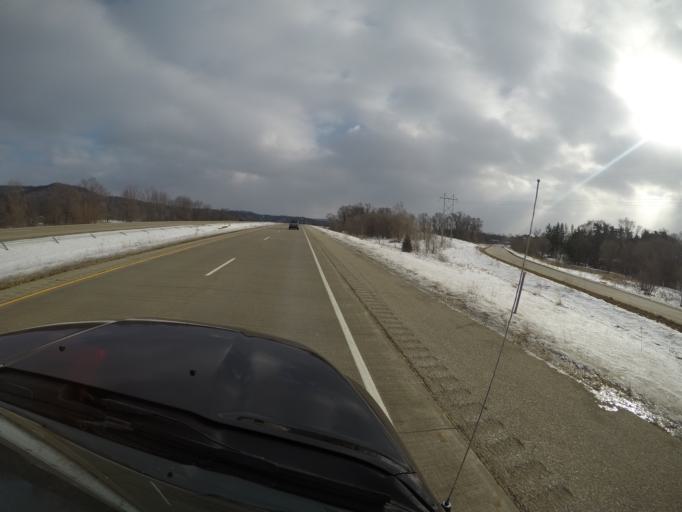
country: US
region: Wisconsin
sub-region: La Crosse County
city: Holmen
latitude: 43.9440
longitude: -91.2605
